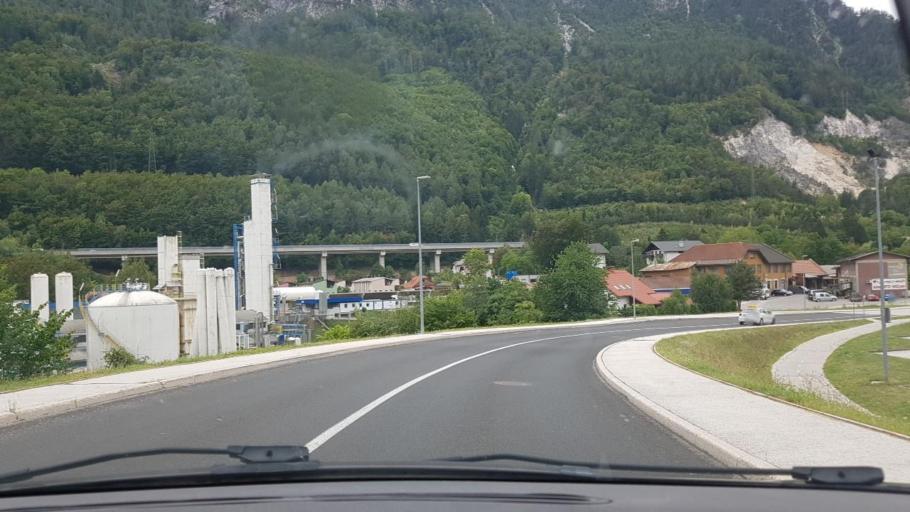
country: SI
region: Jesenice
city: Jesenice
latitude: 46.4319
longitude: 14.0604
